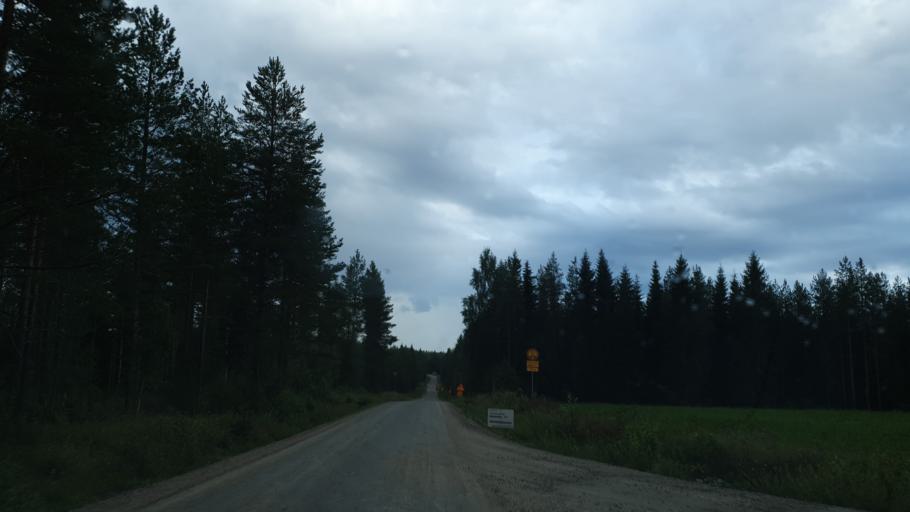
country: FI
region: Kainuu
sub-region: Kehys-Kainuu
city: Kuhmo
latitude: 64.2116
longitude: 29.3695
